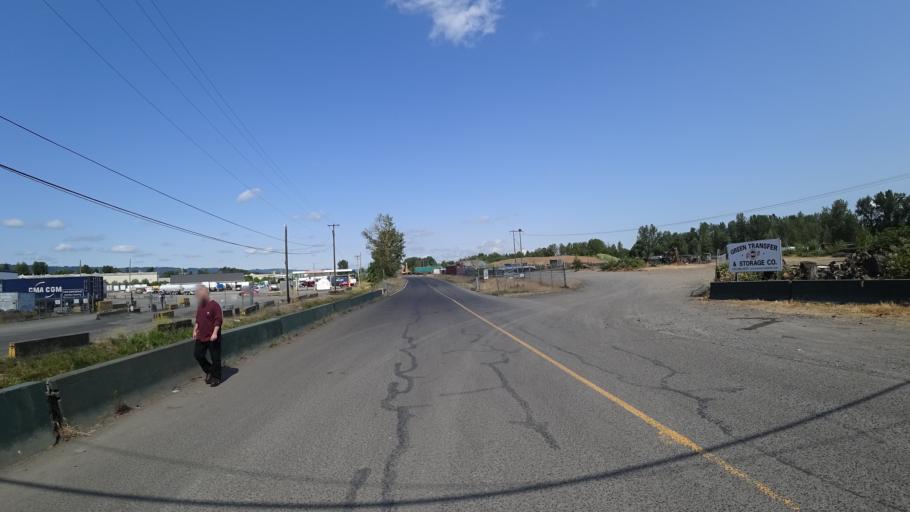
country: US
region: Washington
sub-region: Clark County
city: Vancouver
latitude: 45.5984
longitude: -122.7222
